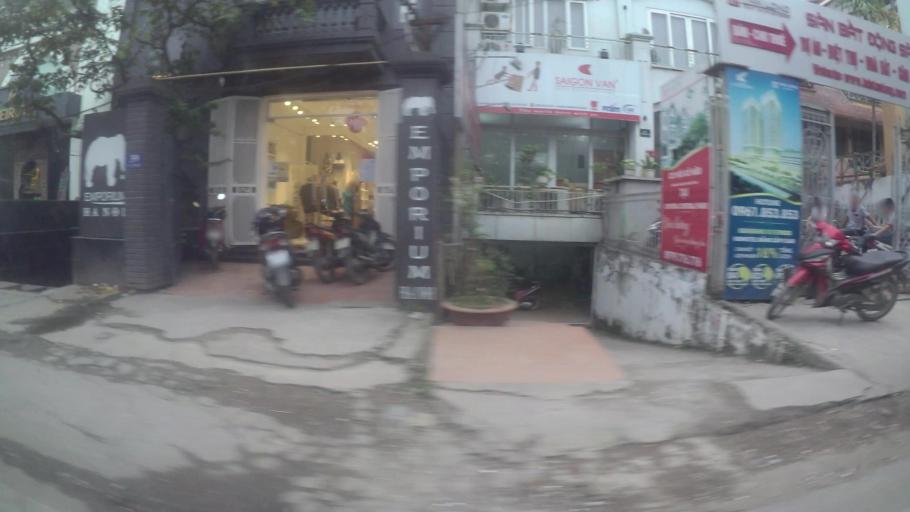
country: VN
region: Ha Noi
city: Tay Ho
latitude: 21.0636
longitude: 105.8287
